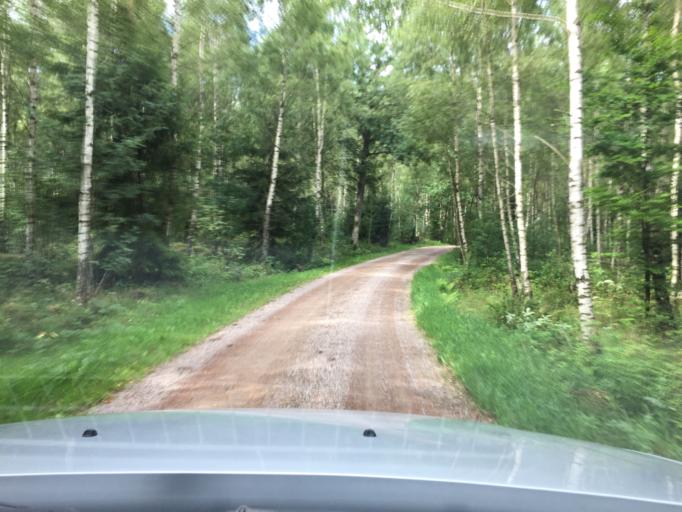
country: SE
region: Skane
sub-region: Hassleholms Kommun
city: Sosdala
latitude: 56.0276
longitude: 13.6397
